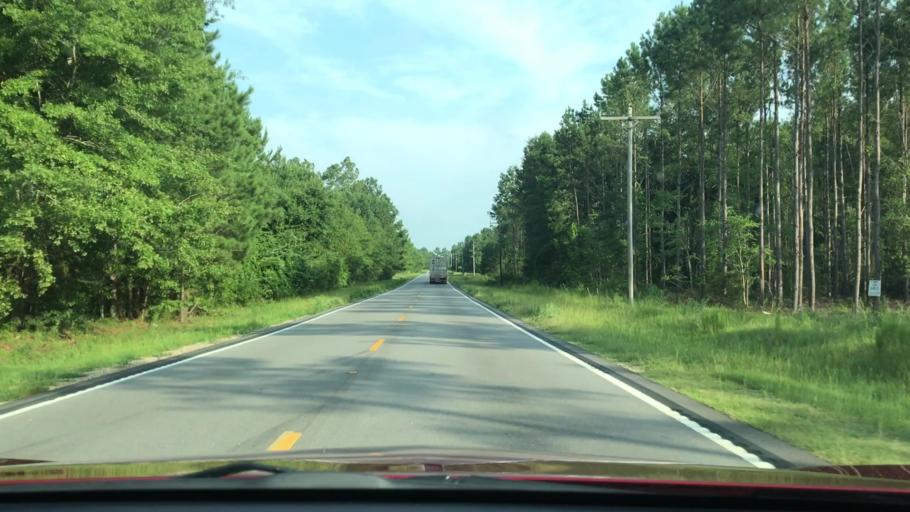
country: US
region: South Carolina
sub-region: Barnwell County
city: Blackville
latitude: 33.5481
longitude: -81.1543
